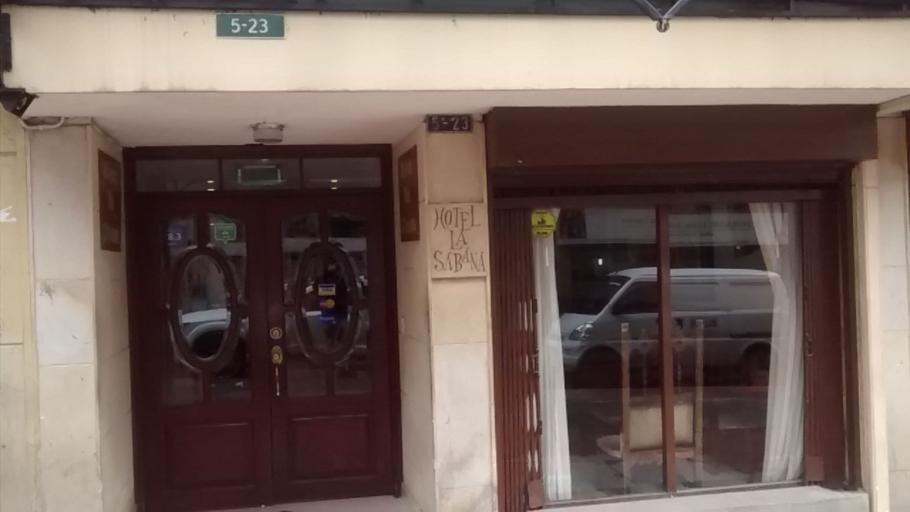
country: CO
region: Bogota D.C.
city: Bogota
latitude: 4.6081
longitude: -74.0688
